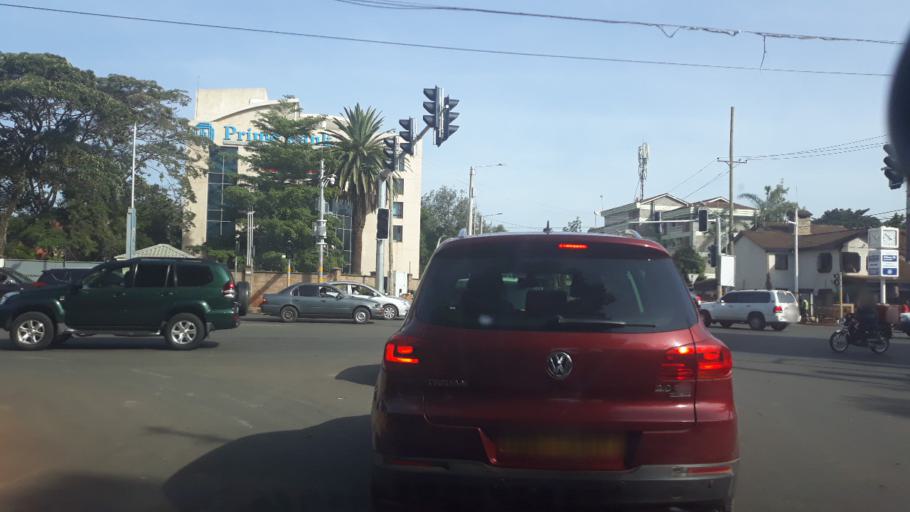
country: KE
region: Nairobi Area
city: Nairobi
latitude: -1.2715
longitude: 36.8013
